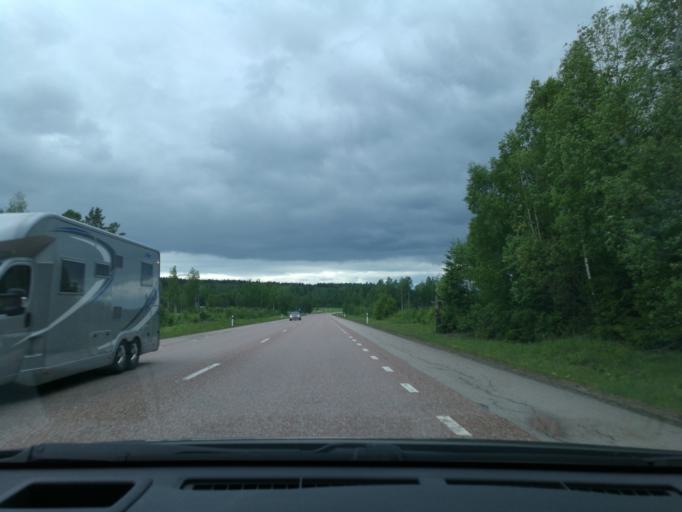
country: SE
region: Dalarna
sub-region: Smedjebackens Kommun
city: Smedjebacken
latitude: 60.1113
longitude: 15.4874
